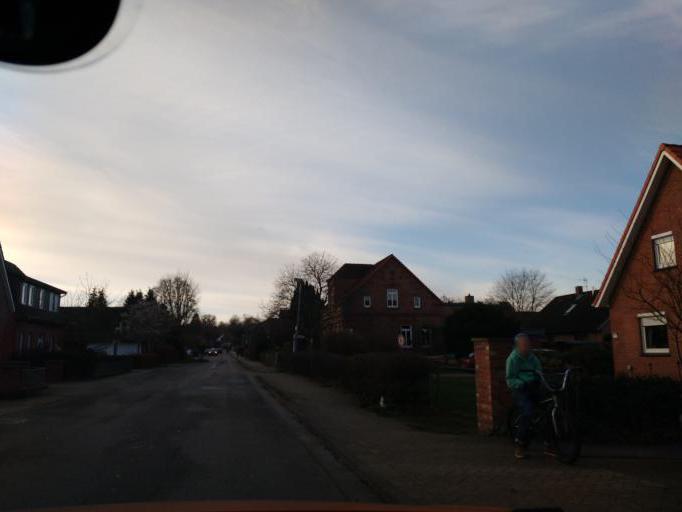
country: DE
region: Lower Saxony
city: Hude
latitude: 53.1109
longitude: 8.4707
